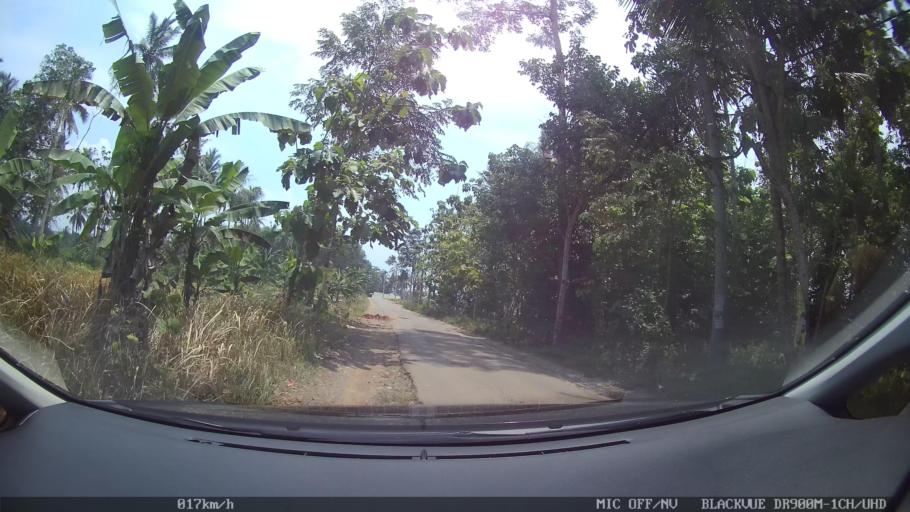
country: ID
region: Lampung
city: Natar
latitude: -5.3152
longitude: 105.2474
